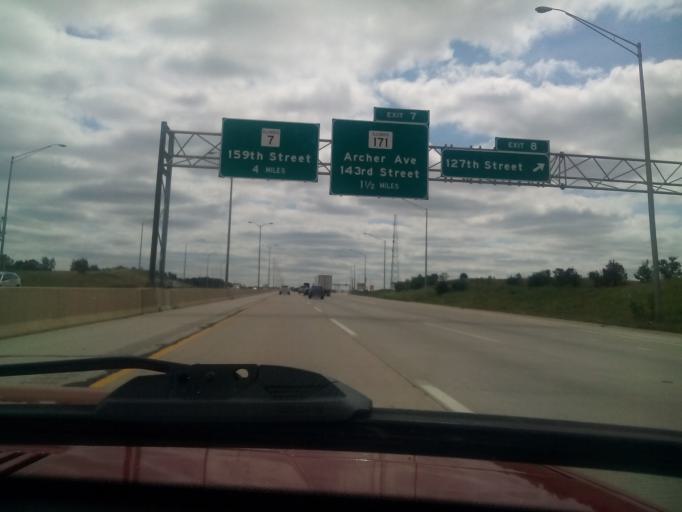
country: US
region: Illinois
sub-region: Cook County
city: Lemont
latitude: 41.6626
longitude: -88.0236
